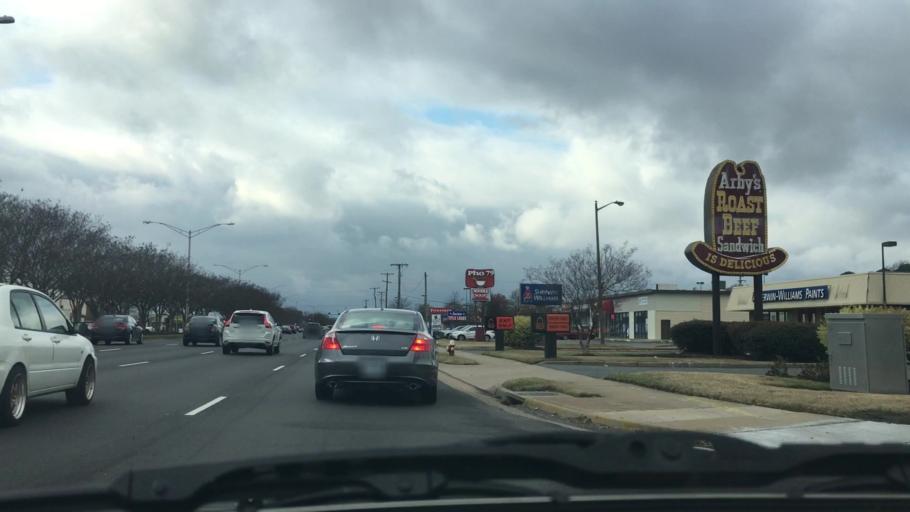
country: US
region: Virginia
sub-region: City of Chesapeake
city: Chesapeake
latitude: 36.8438
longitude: -76.1421
